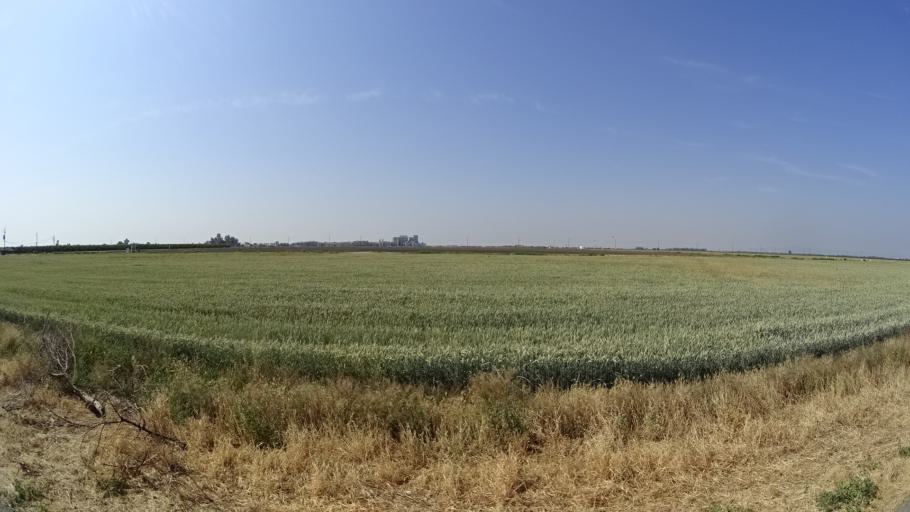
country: US
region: California
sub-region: Kings County
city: Lemoore
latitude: 36.3134
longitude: -119.8197
